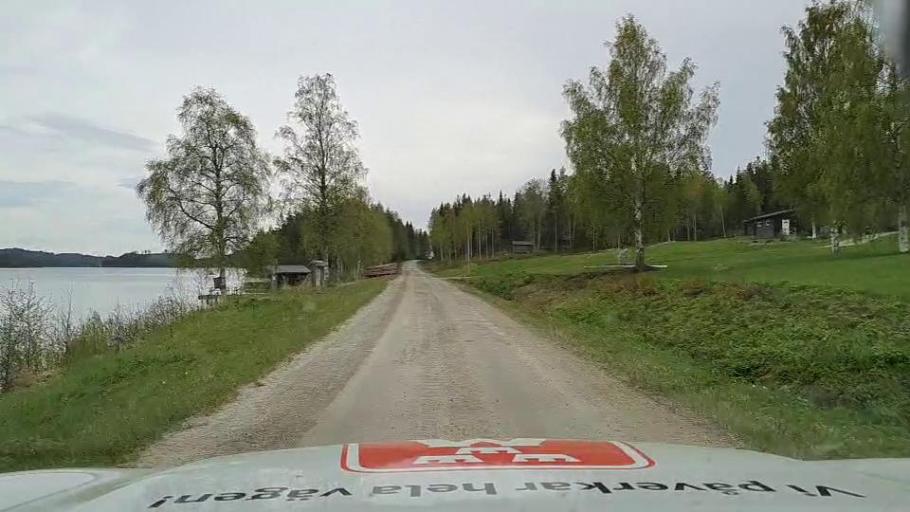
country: SE
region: Jaemtland
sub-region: Bergs Kommun
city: Hoverberg
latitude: 62.6873
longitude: 14.7745
